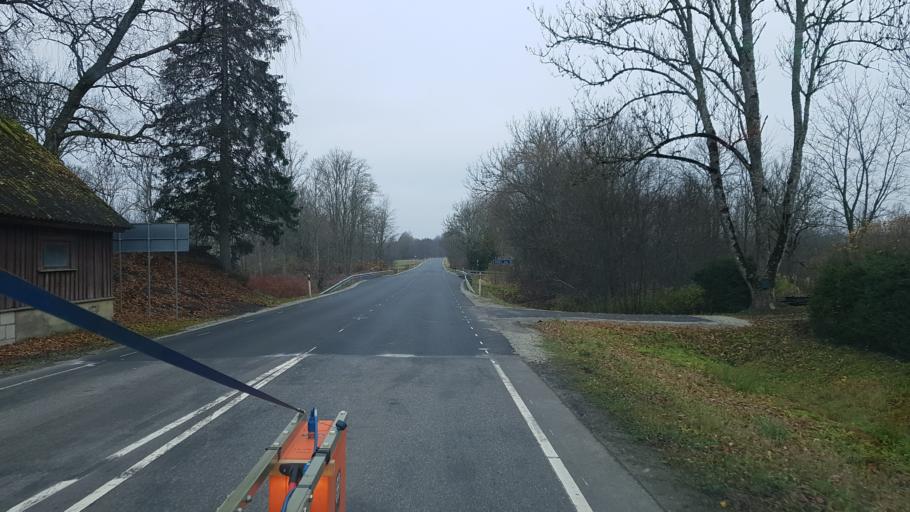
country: EE
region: Paernumaa
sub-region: Vaendra vald (alev)
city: Vandra
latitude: 58.8220
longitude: 25.1403
